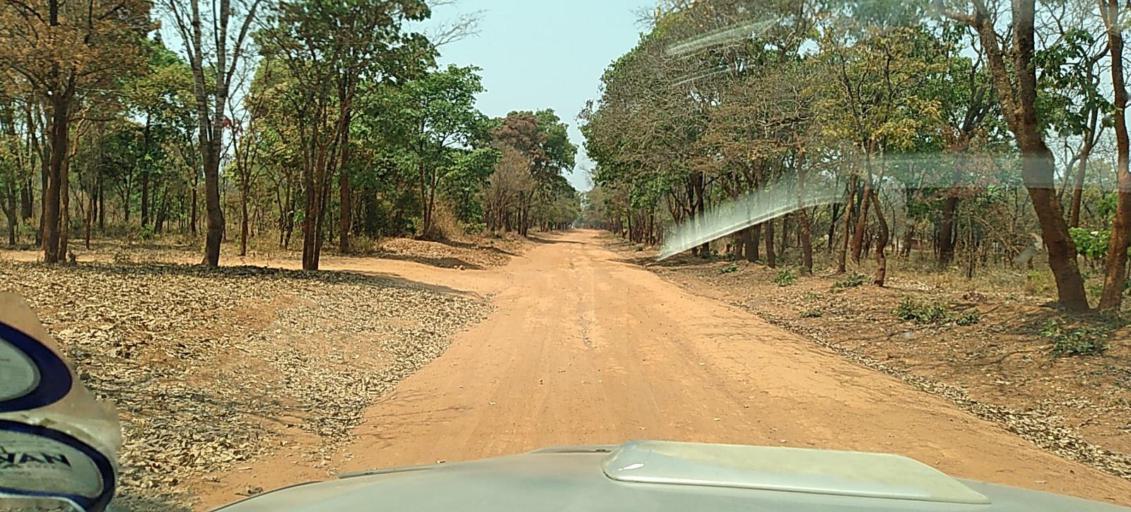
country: ZM
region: North-Western
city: Kasempa
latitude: -13.5658
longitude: 26.0946
